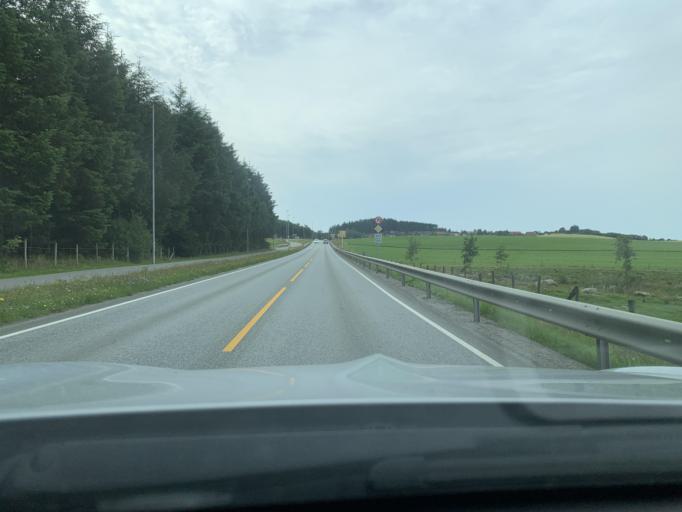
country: NO
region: Rogaland
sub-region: Time
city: Bryne
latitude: 58.7368
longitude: 5.6855
